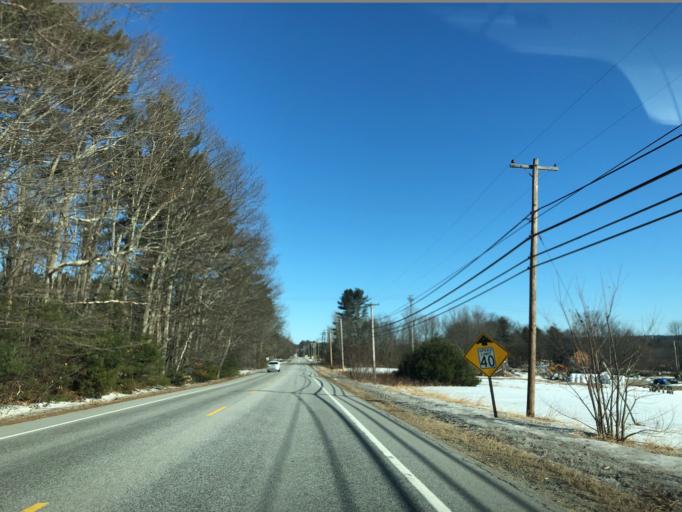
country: US
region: Maine
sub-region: Cumberland County
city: South Windham
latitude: 43.7739
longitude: -70.4186
